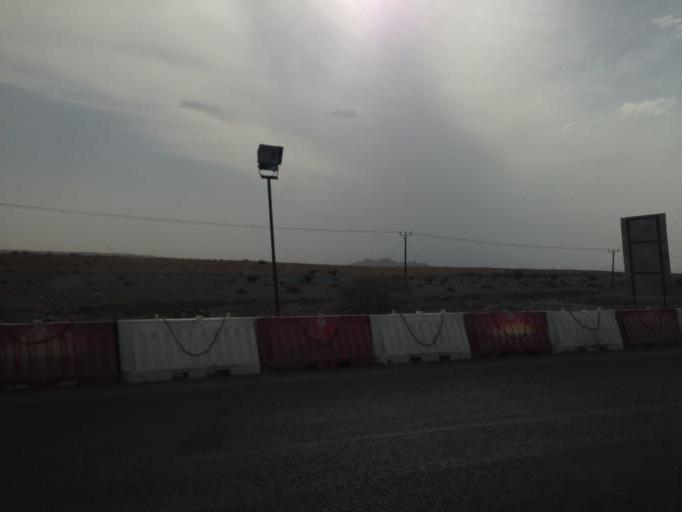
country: OM
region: Ash Sharqiyah
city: Al Qabil
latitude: 22.5369
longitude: 58.7298
